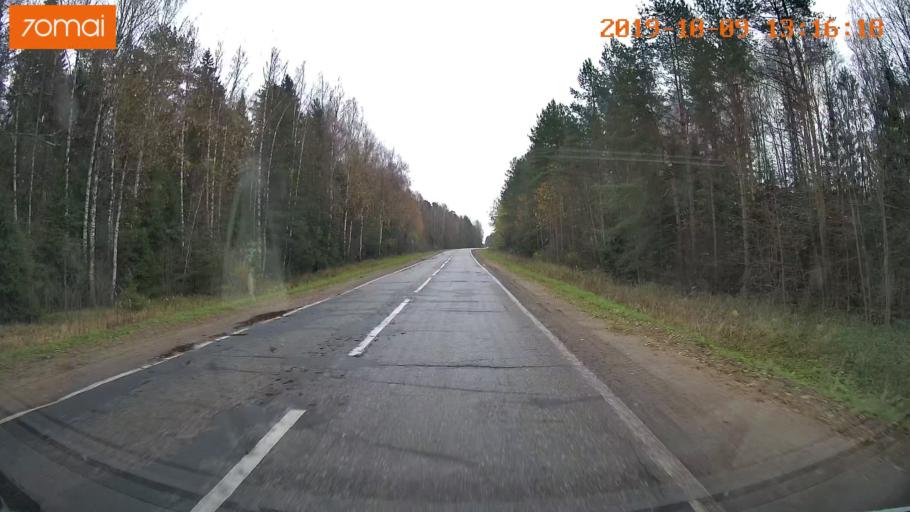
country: RU
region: Jaroslavl
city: Lyubim
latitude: 58.3622
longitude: 40.7639
